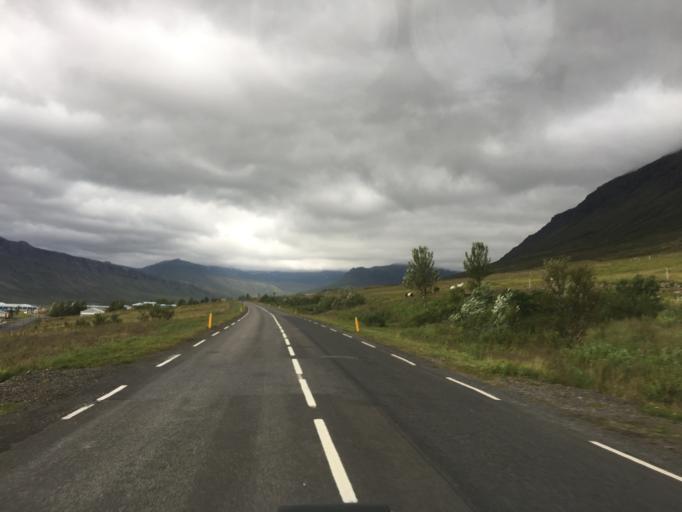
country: IS
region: East
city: Neskaupstadur
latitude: 65.1446
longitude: -13.7313
